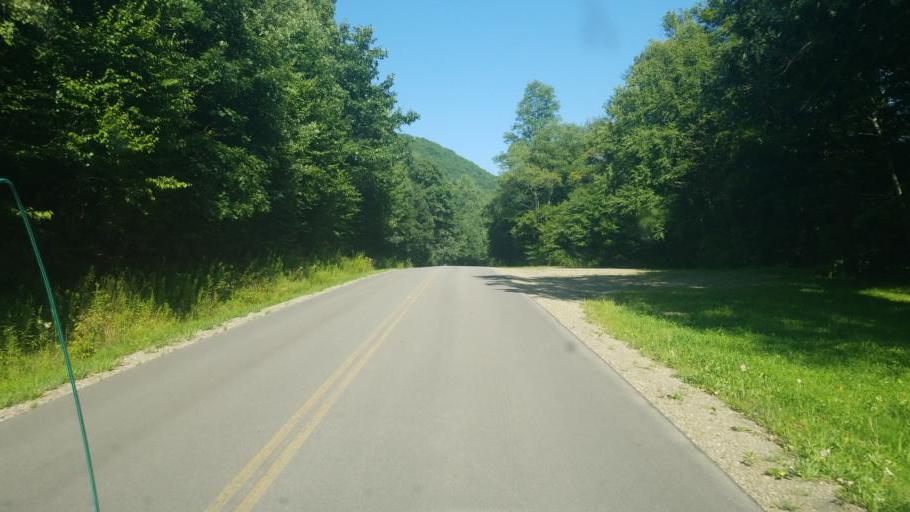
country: US
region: New York
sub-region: Allegany County
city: Wellsville
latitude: 42.0150
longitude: -78.0042
